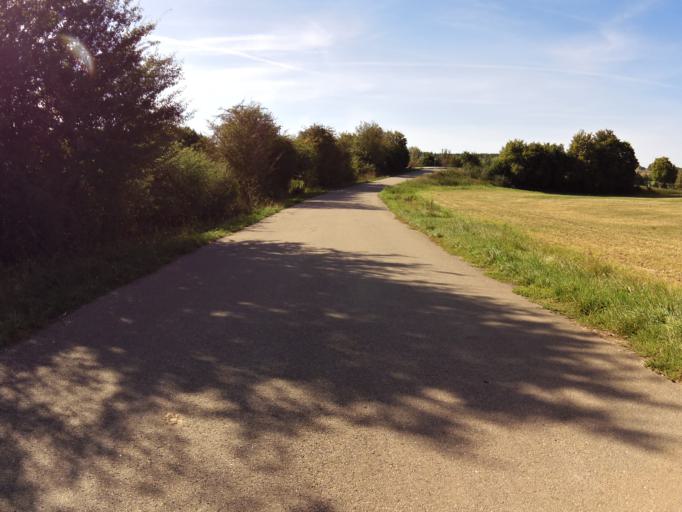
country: DE
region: Baden-Wuerttemberg
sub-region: Freiburg Region
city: Deisslingen
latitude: 48.0926
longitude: 8.5854
